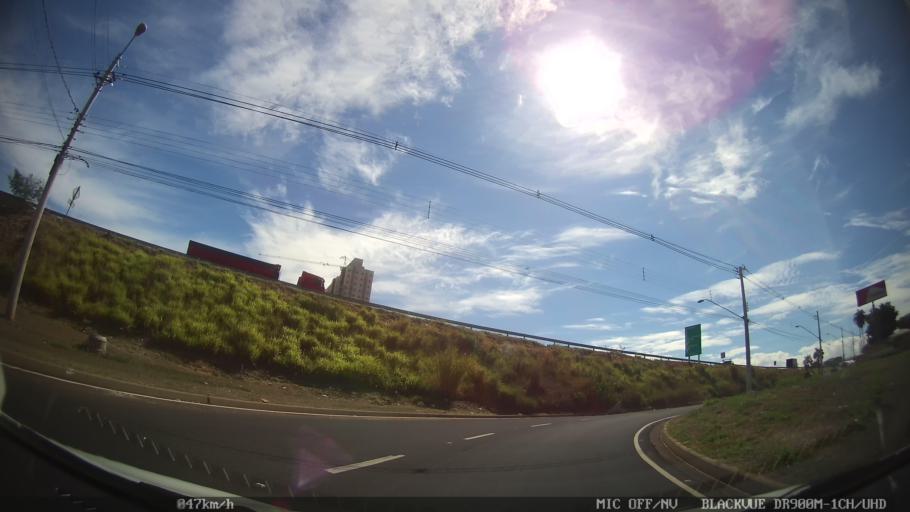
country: BR
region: Sao Paulo
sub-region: Sao Jose Do Rio Preto
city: Sao Jose do Rio Preto
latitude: -20.8377
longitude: -49.3668
